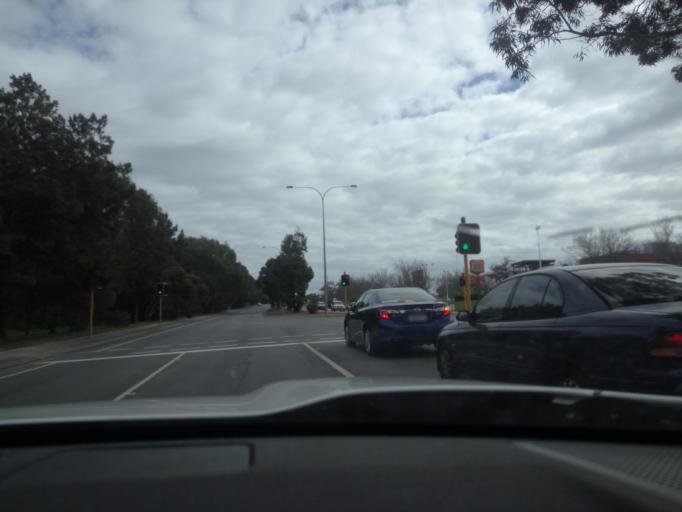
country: AU
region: Western Australia
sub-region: City of Cockburn
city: South Lake
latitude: -32.1088
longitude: 115.8289
